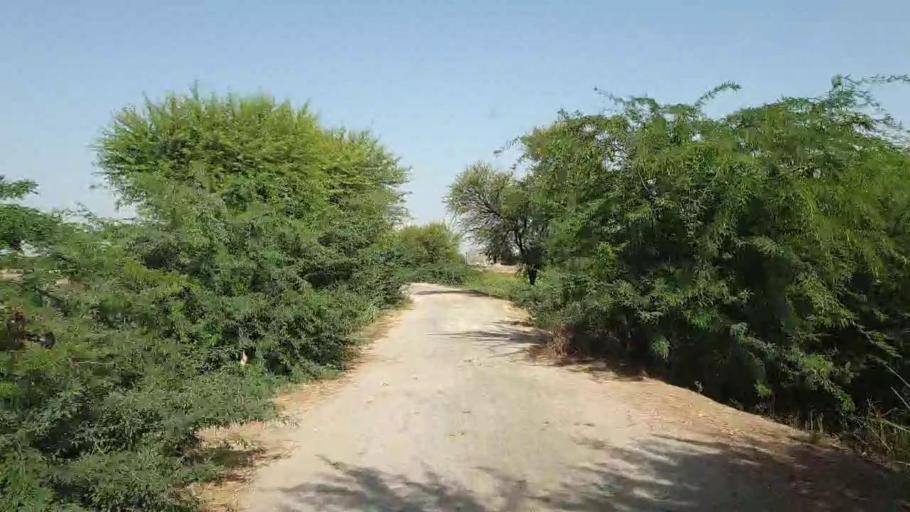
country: PK
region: Sindh
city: Tando Bago
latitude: 24.7654
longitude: 69.0230
